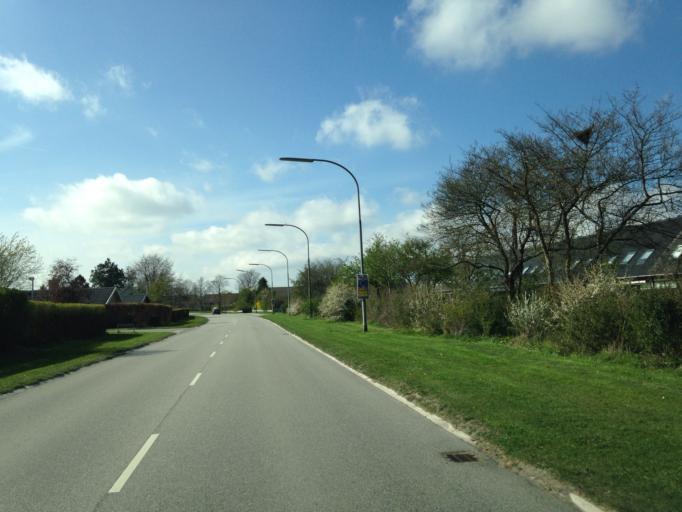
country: DK
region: Zealand
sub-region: Greve Kommune
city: Greve
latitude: 55.5841
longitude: 12.2794
